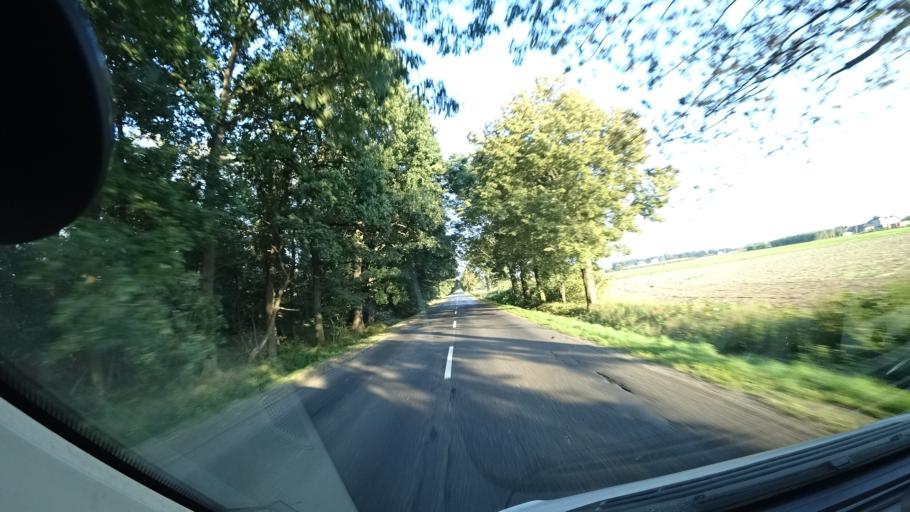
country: PL
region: Opole Voivodeship
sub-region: Powiat kedzierzynsko-kozielski
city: Bierawa
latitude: 50.2949
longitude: 18.2413
